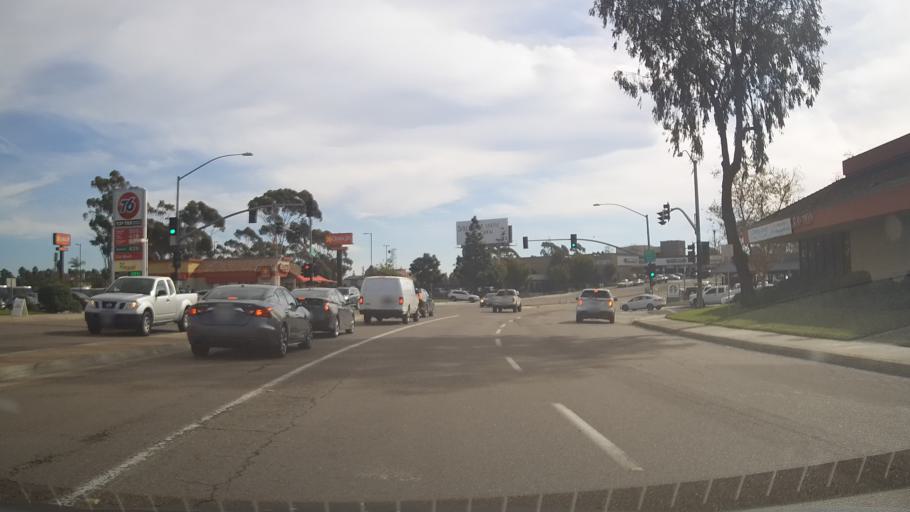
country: US
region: California
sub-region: San Diego County
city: San Diego
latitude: 32.8140
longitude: -117.1532
